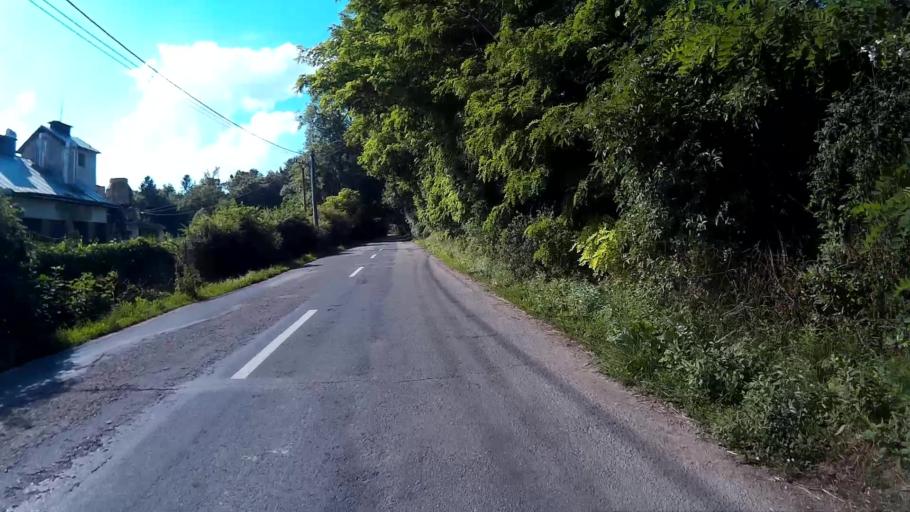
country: CZ
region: South Moravian
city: Sitborice
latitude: 48.9916
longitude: 16.7864
